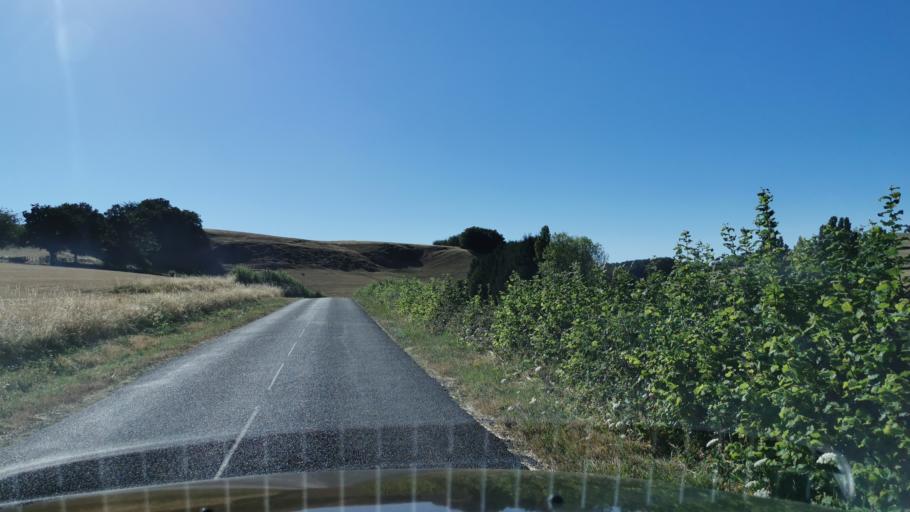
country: FR
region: Bourgogne
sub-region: Departement de Saone-et-Loire
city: Montcenis
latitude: 46.7999
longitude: 4.3624
